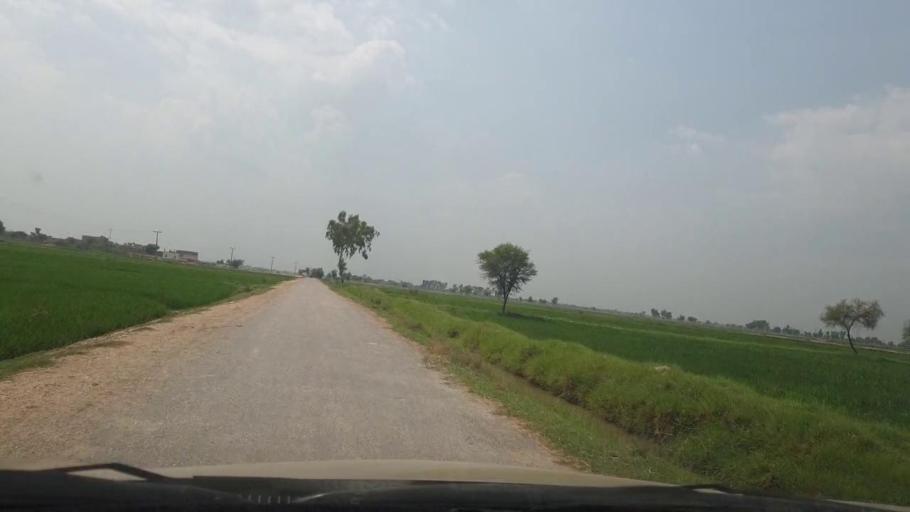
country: PK
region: Sindh
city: Ratodero
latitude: 27.7019
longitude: 68.2563
